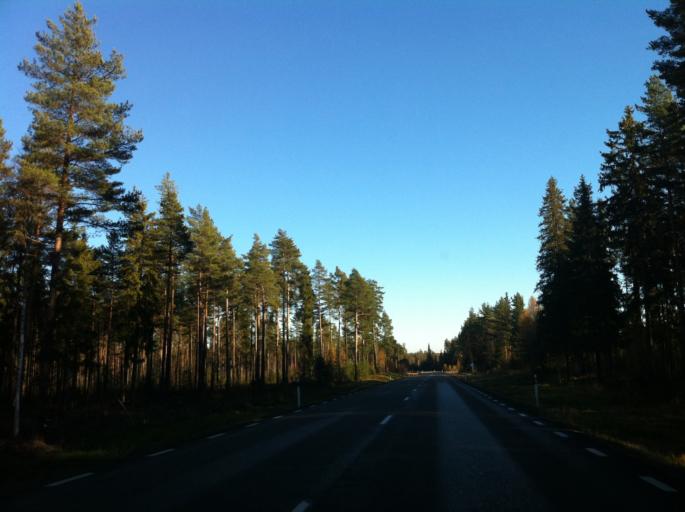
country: SE
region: Dalarna
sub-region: Leksand Municipality
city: Siljansnas
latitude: 60.9212
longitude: 14.8481
